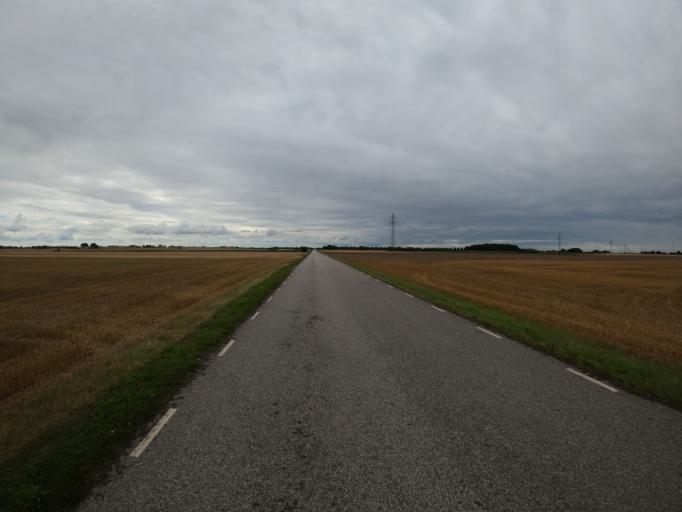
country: SE
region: Skane
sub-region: Lunds Kommun
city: Lund
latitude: 55.7607
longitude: 13.1727
